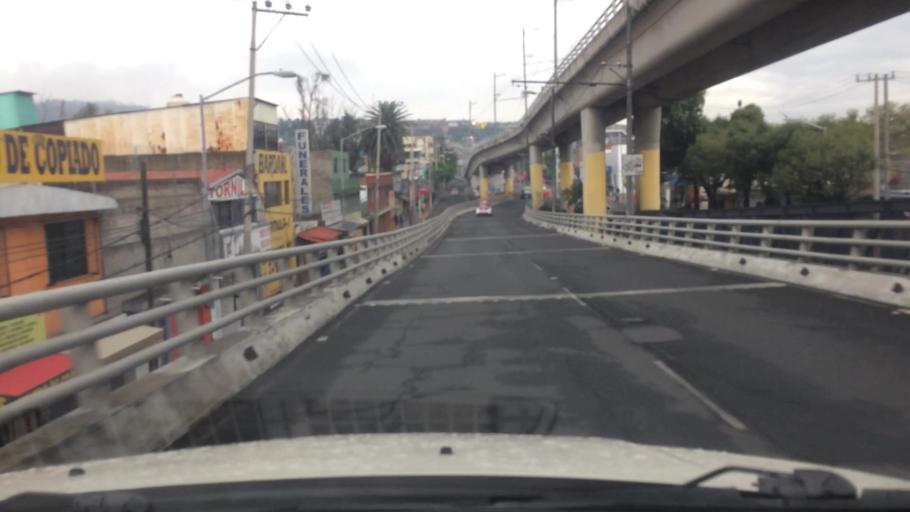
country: MX
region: Mexico City
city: Iztapalapa
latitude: 19.3387
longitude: -99.1123
